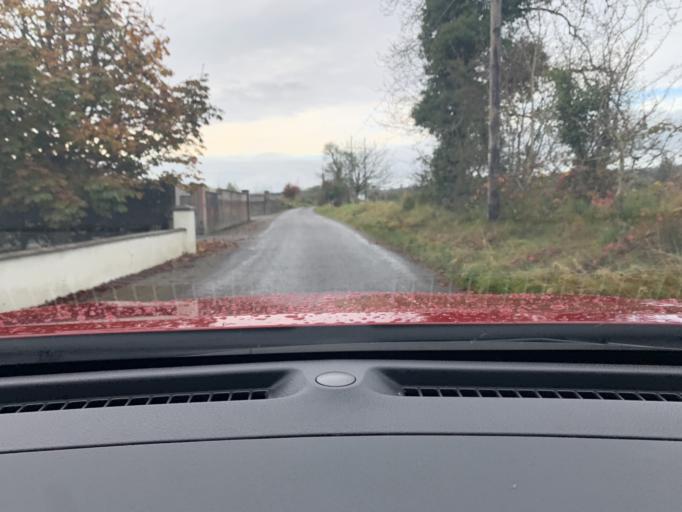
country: IE
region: Connaught
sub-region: Roscommon
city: Ballaghaderreen
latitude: 53.9119
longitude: -8.5629
